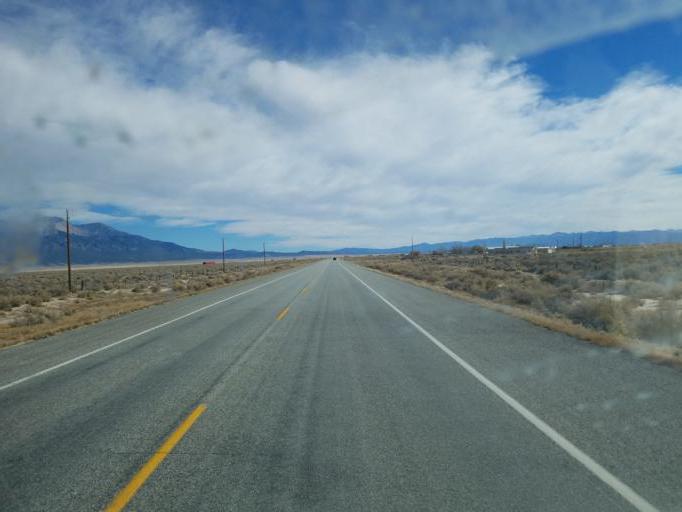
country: US
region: Colorado
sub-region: Alamosa County
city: Alamosa East
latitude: 37.4745
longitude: -105.7140
